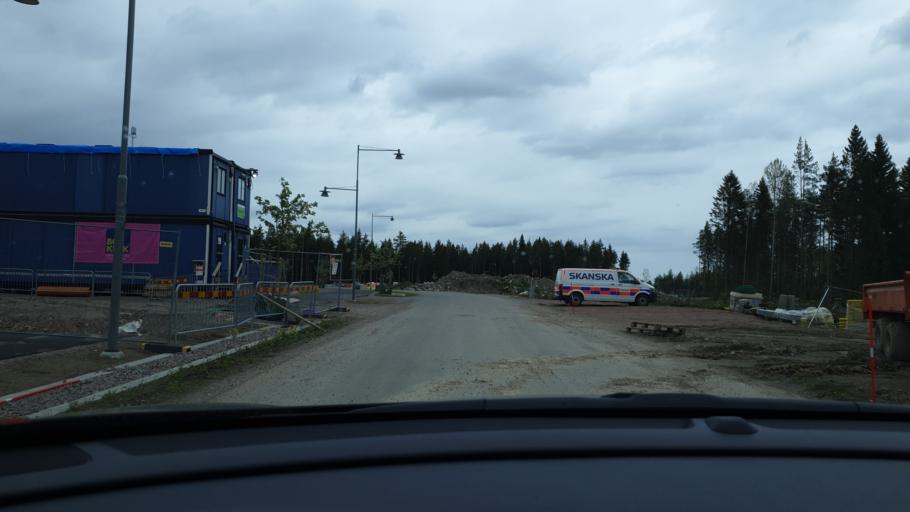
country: SE
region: Gaevleborg
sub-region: Gavle Kommun
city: Gavle
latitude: 60.6407
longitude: 17.1538
